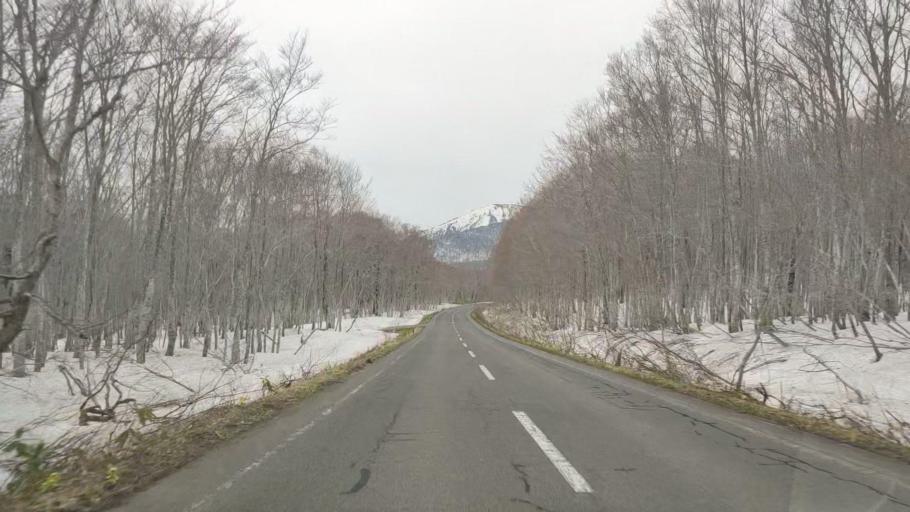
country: JP
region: Aomori
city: Aomori Shi
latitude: 40.6368
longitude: 140.9307
